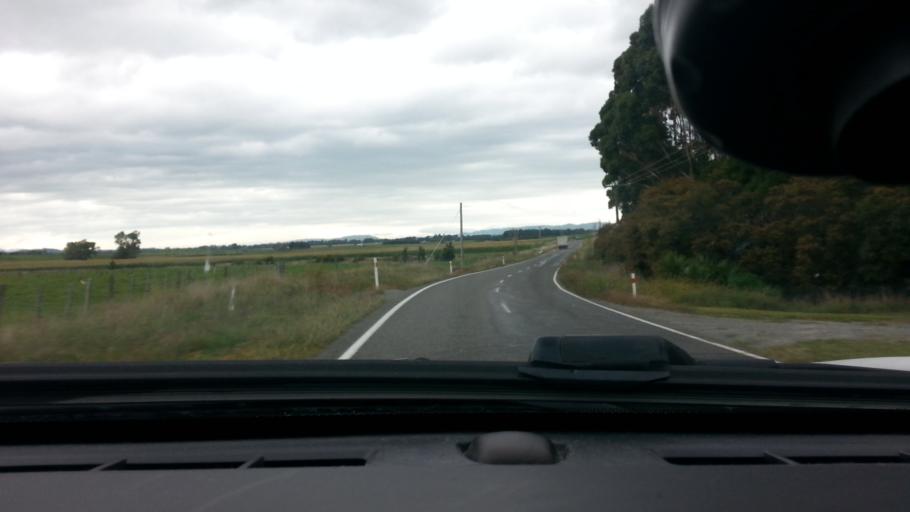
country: NZ
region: Wellington
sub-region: South Wairarapa District
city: Waipawa
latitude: -41.2781
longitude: 175.3575
